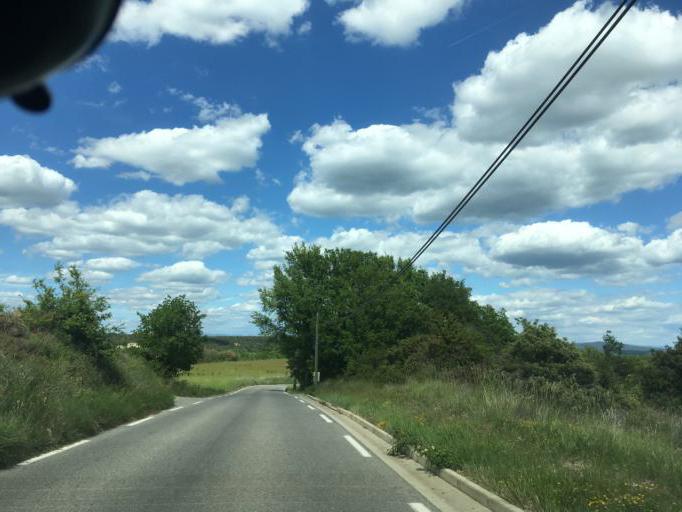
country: FR
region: Provence-Alpes-Cote d'Azur
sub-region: Departement du Var
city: Ginasservis
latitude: 43.5952
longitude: 5.8647
